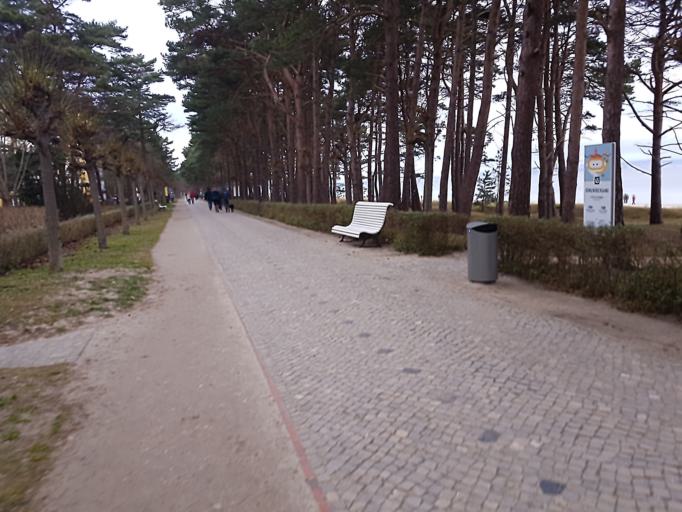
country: DE
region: Mecklenburg-Vorpommern
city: Ostseebad Binz
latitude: 54.4123
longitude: 13.5992
